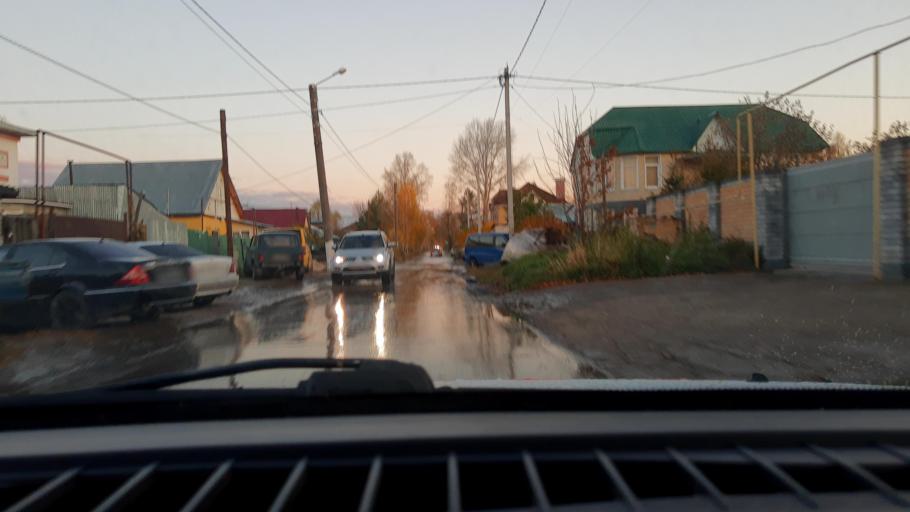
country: RU
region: Nizjnij Novgorod
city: Gorbatovka
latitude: 56.3333
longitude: 43.8308
